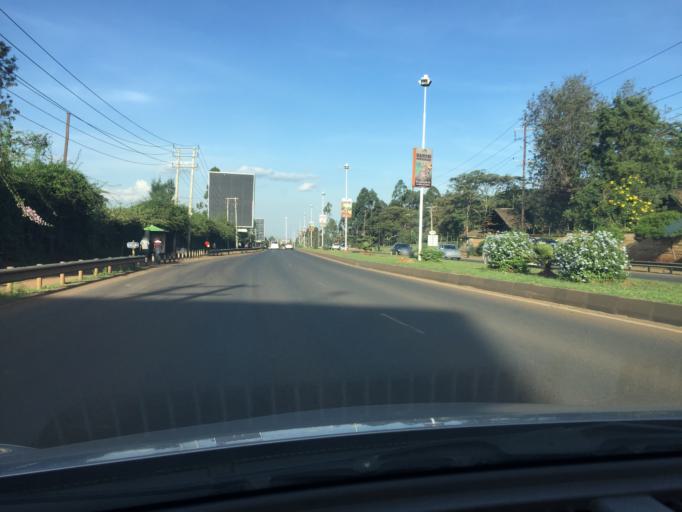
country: KE
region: Nairobi Area
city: Nairobi
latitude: -1.3344
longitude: 36.7788
